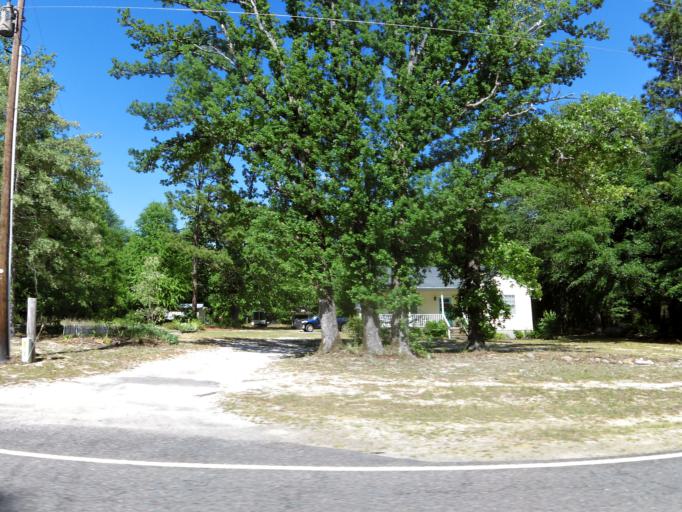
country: US
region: South Carolina
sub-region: Barnwell County
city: Williston
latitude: 33.4235
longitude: -81.4788
